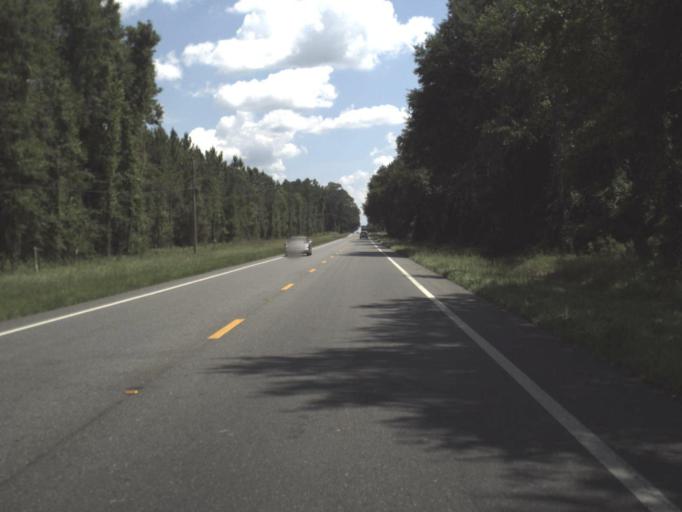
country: US
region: Florida
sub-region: Columbia County
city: Watertown
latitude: 30.0717
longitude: -82.6005
